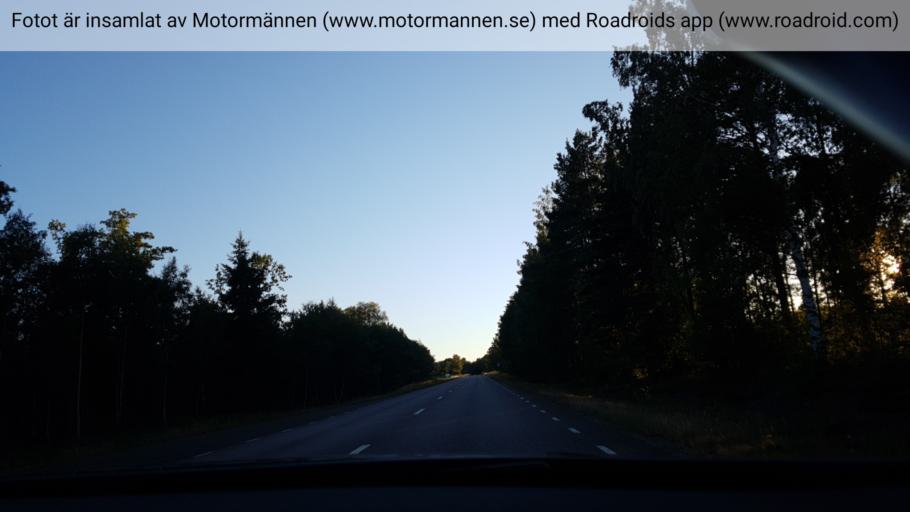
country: SE
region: Vaestra Goetaland
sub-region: Hjo Kommun
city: Hjo
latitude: 58.3217
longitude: 14.2950
